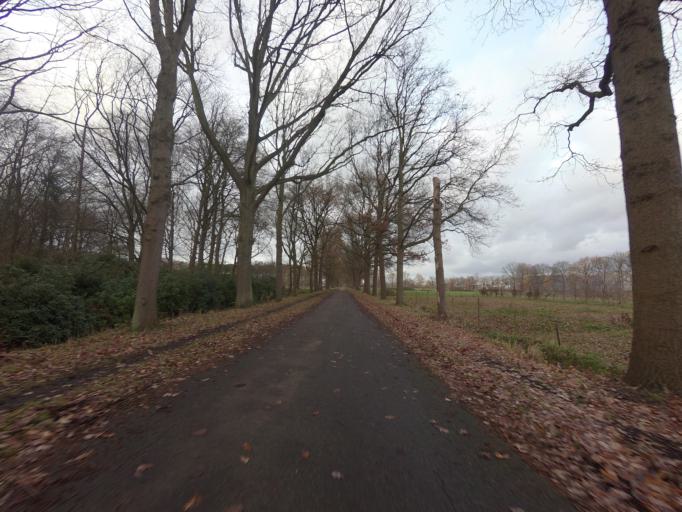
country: BE
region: Flanders
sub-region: Provincie Antwerpen
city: Hemiksem
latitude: 51.1546
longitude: 4.3619
